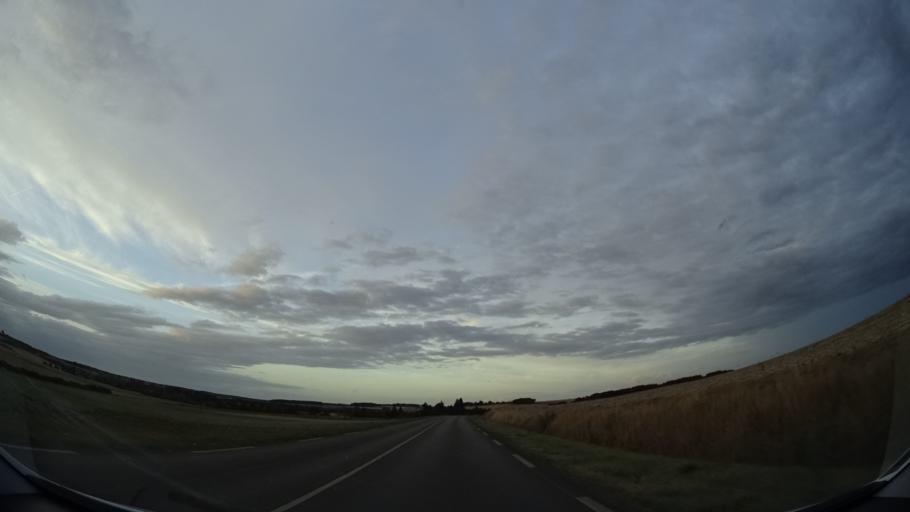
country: FR
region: Bourgogne
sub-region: Departement de l'Yonne
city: Saint-Julien-du-Sault
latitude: 47.9349
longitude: 3.2320
